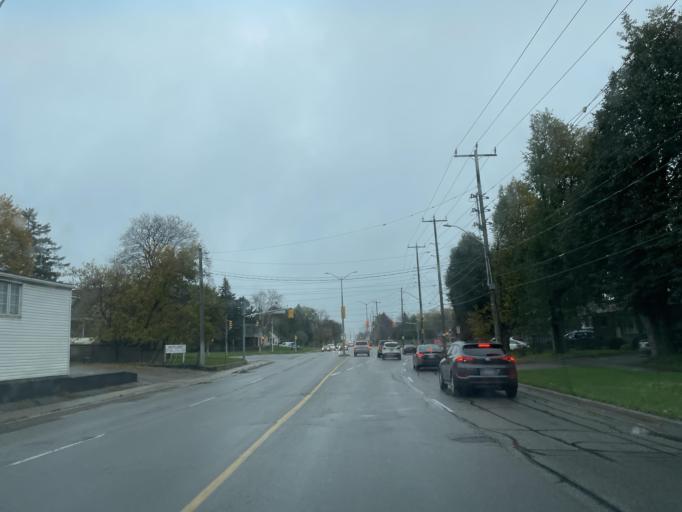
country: CA
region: Ontario
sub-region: Wellington County
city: Guelph
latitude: 43.5720
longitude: -80.2520
